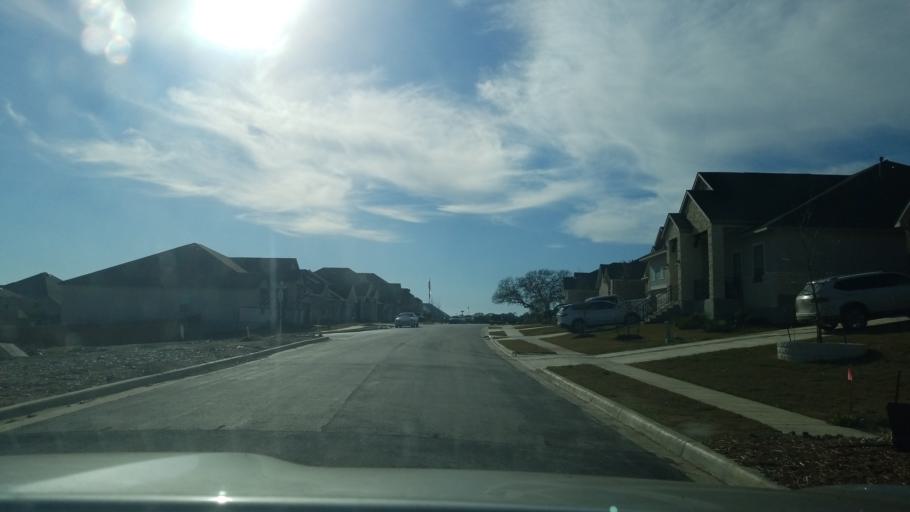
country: US
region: Texas
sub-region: Comal County
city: Canyon Lake
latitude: 29.7811
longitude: -98.2854
